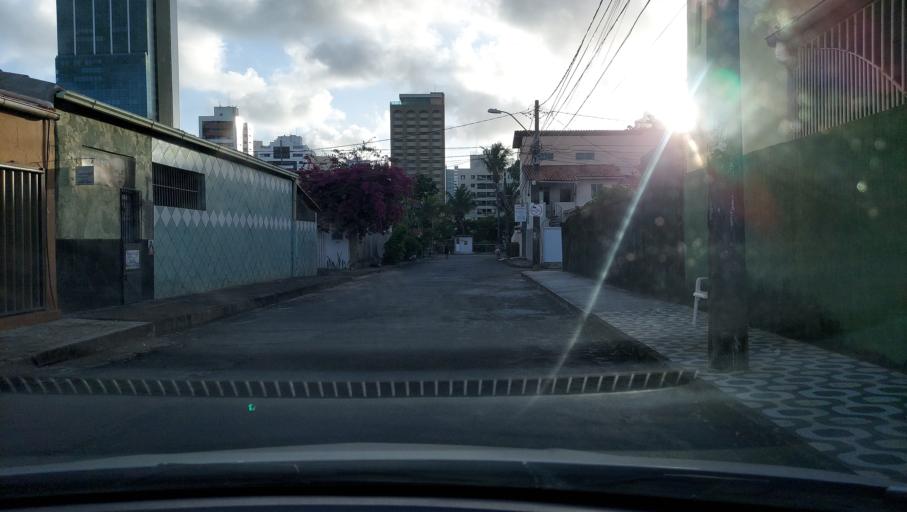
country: BR
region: Bahia
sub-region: Salvador
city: Salvador
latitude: -12.9848
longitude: -38.4471
